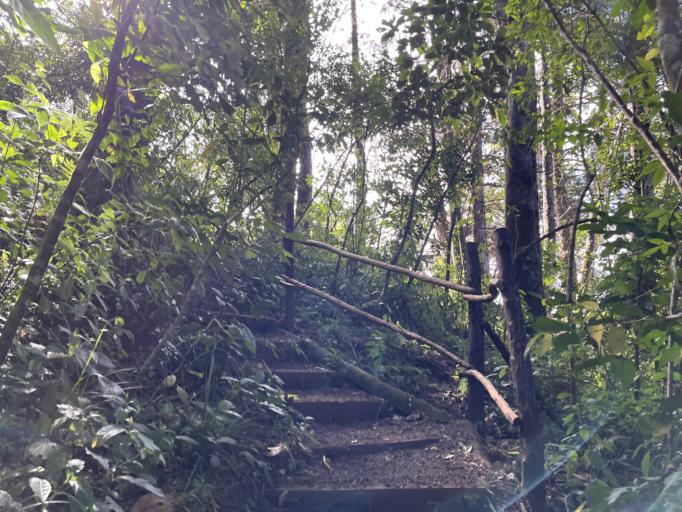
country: CR
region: Heredia
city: Angeles
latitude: 10.0393
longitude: -84.0427
